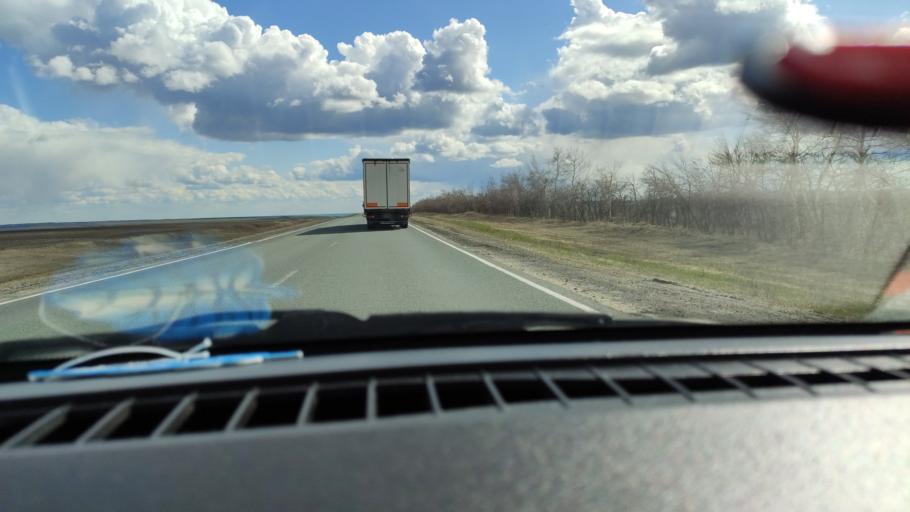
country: RU
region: Saratov
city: Dukhovnitskoye
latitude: 52.7878
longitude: 48.2328
